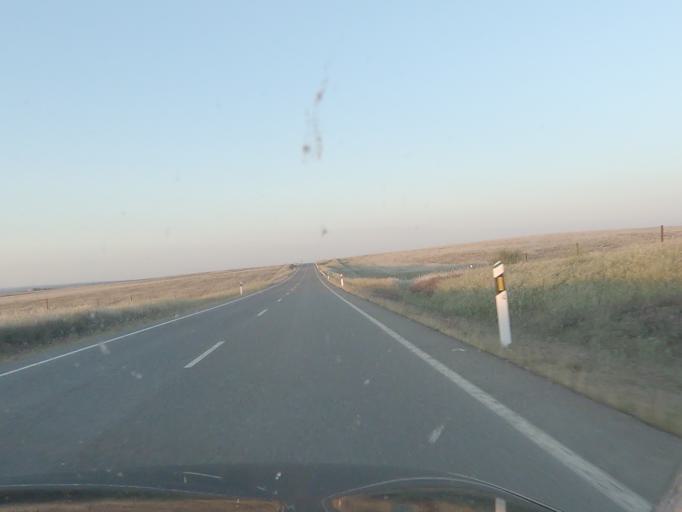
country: ES
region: Extremadura
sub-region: Provincia de Caceres
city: Alcantara
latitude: 39.6286
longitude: -6.9274
